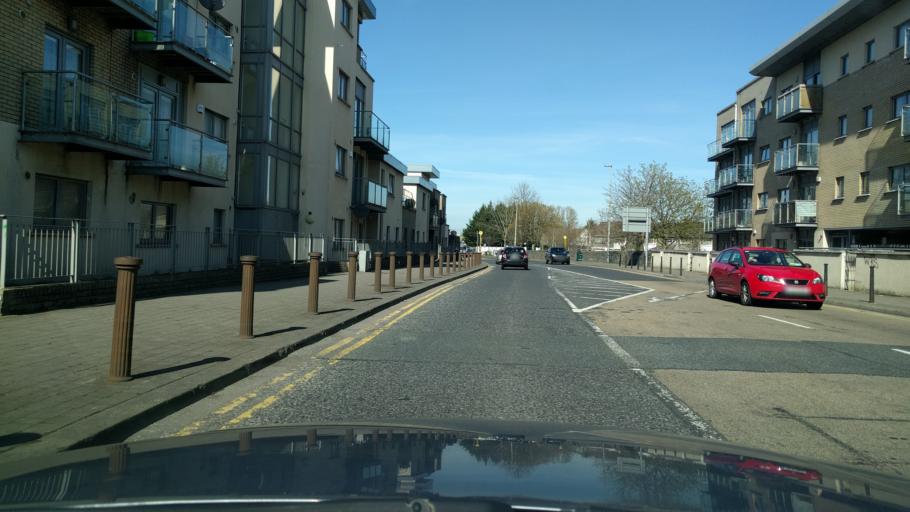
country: IE
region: Leinster
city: Tallaght
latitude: 53.2884
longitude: -6.3576
